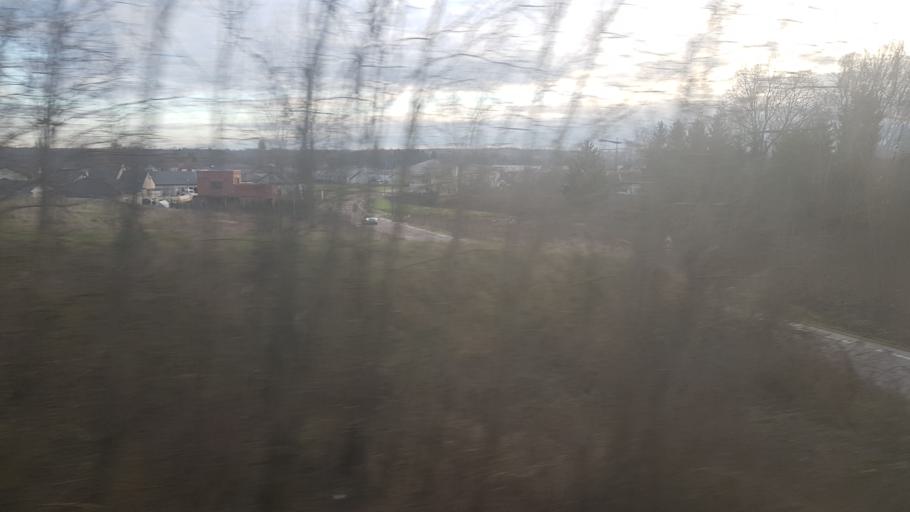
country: FR
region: Lorraine
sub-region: Departement des Vosges
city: Igney
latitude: 48.2610
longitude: 6.4021
